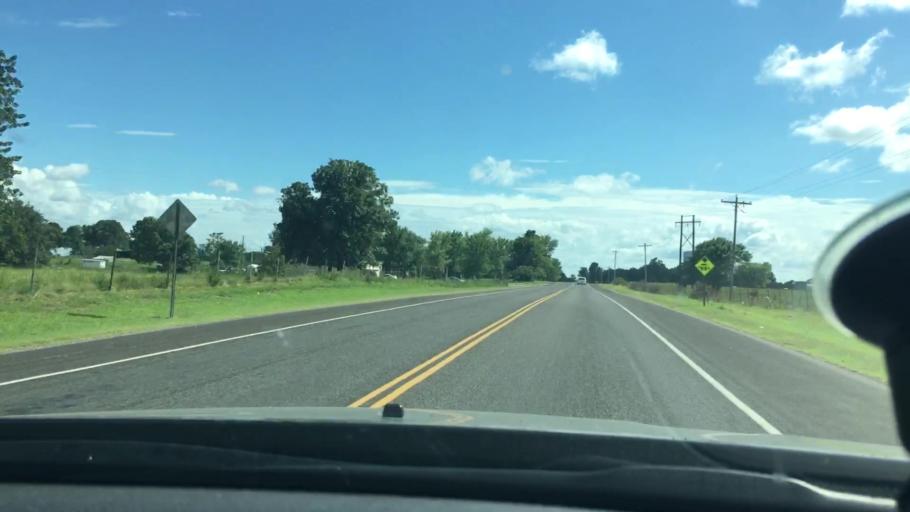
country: US
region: Oklahoma
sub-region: Sequoyah County
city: Vian
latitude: 35.5725
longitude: -94.9853
